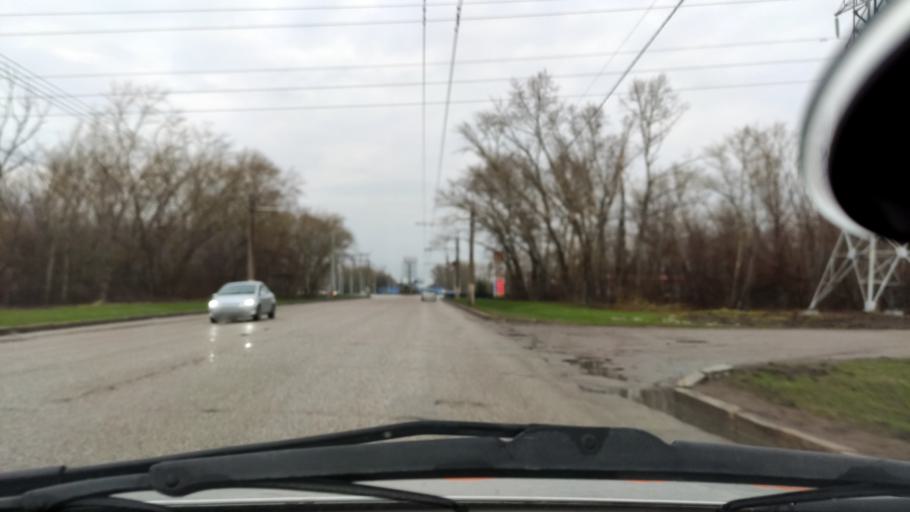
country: RU
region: Bashkortostan
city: Sterlitamak
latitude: 53.6611
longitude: 55.9490
